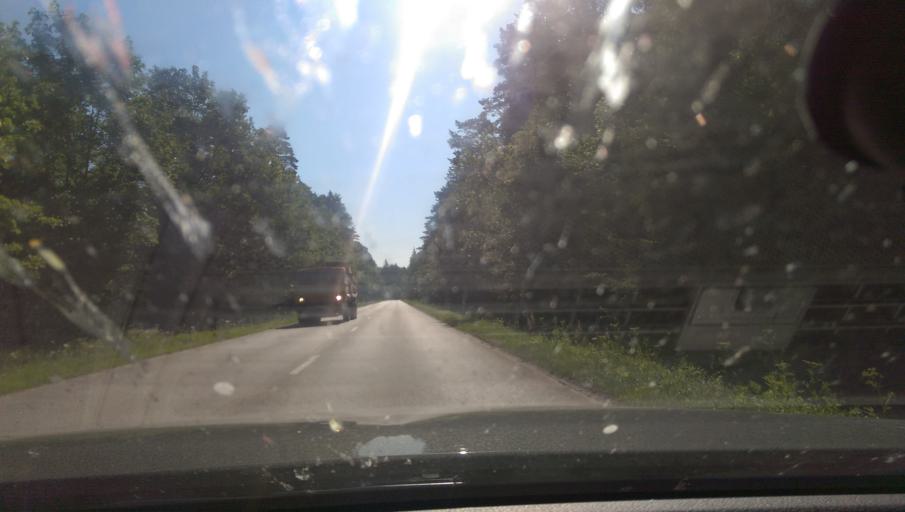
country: LT
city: Priekule
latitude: 55.6364
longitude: 21.3273
